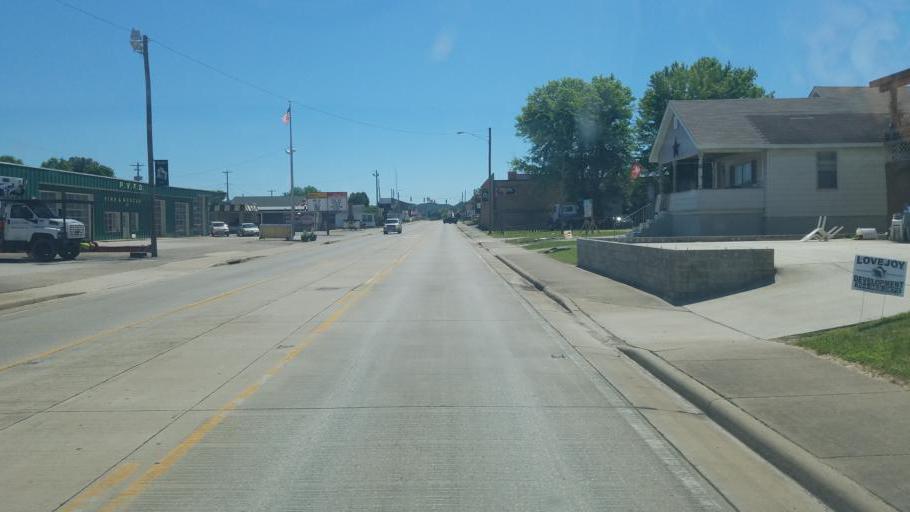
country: US
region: West Virginia
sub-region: Cabell County
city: Pea Ridge
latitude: 38.4381
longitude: -82.3815
